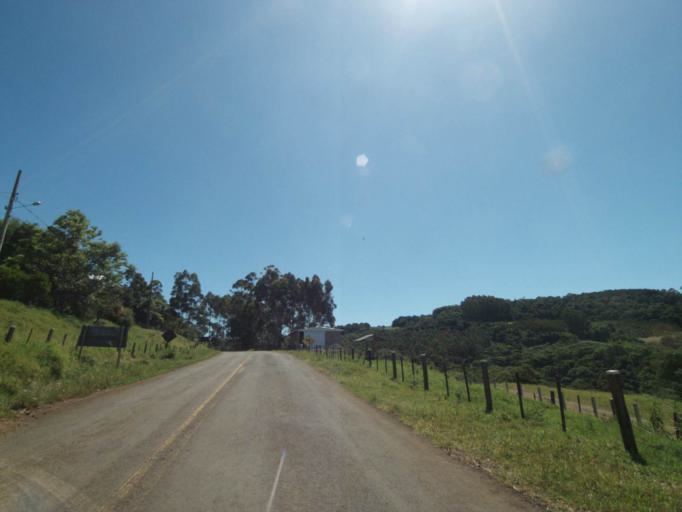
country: BR
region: Parana
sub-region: Ampere
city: Ampere
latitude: -26.1797
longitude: -53.3631
